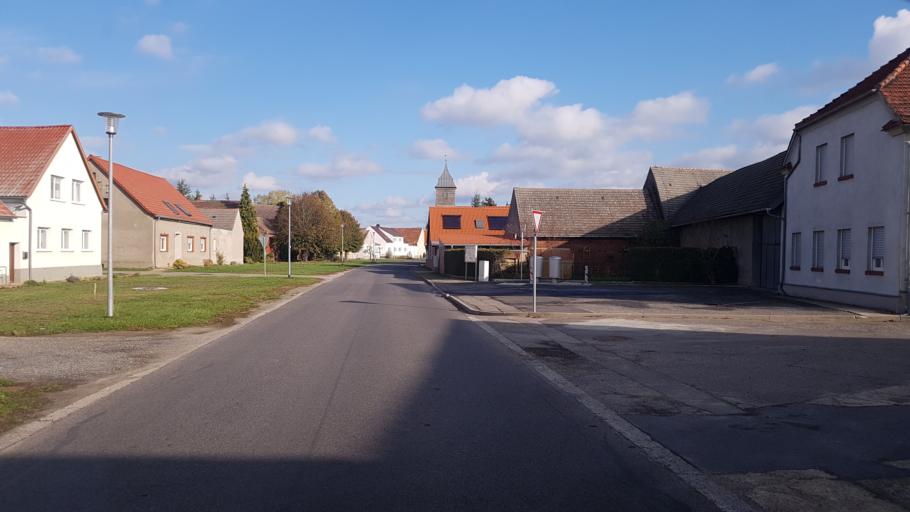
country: DE
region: Brandenburg
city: Schonewalde
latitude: 51.6917
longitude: 13.5339
